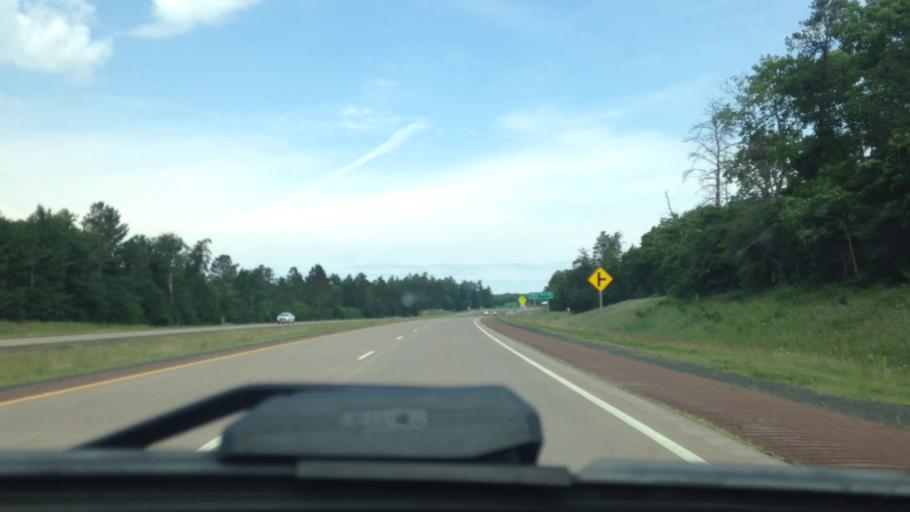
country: US
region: Wisconsin
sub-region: Douglas County
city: Lake Nebagamon
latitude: 46.3411
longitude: -91.8330
